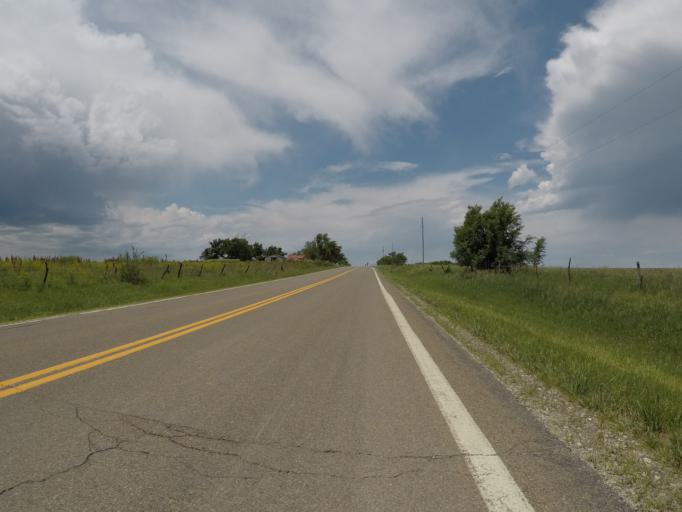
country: US
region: Kansas
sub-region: Wabaunsee County
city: Alma
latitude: 38.8548
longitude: -96.4124
